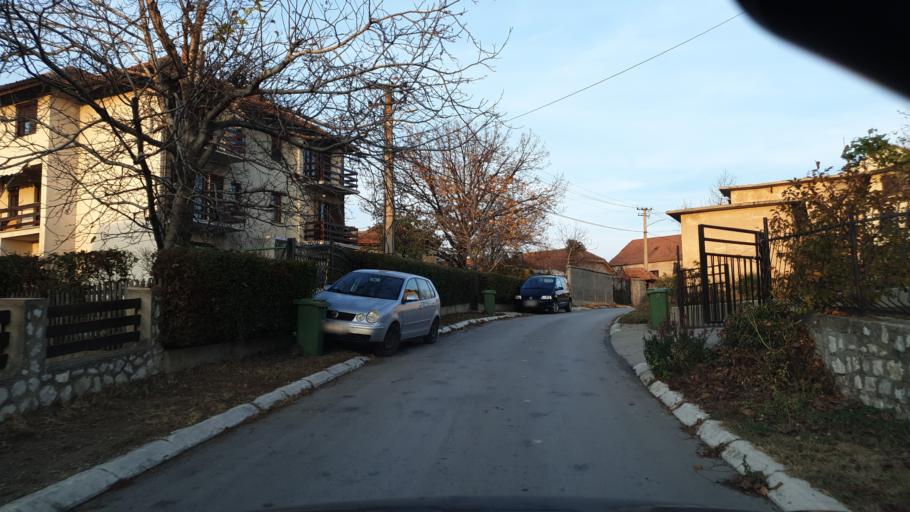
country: RS
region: Central Serbia
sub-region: Borski Okrug
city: Bor
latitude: 44.0618
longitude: 22.0921
